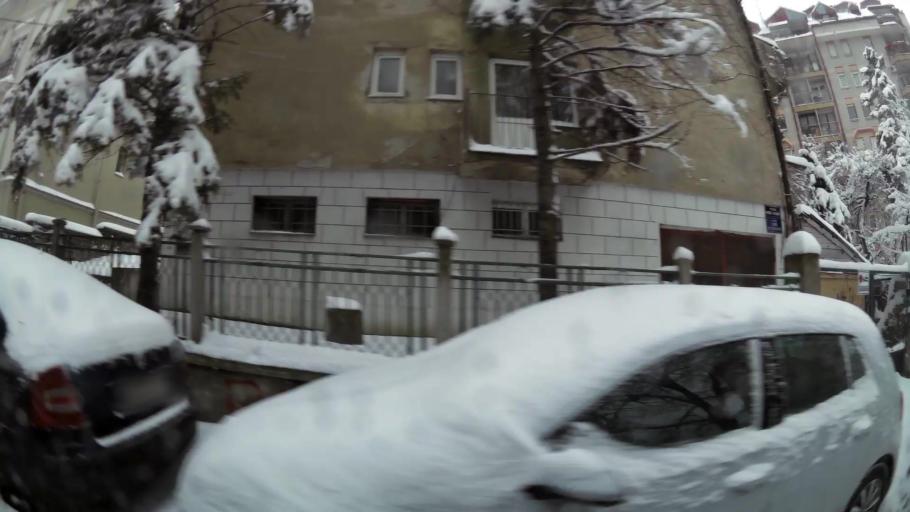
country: RS
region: Central Serbia
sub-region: Belgrade
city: Vracar
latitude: 44.7917
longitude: 20.4725
